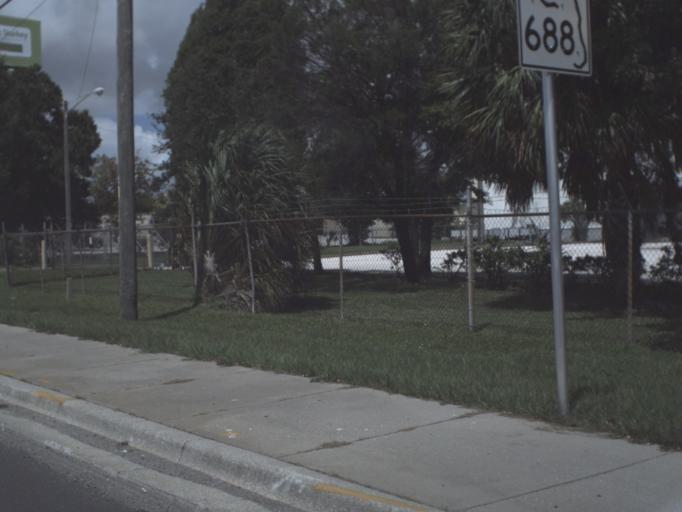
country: US
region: Florida
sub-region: Pinellas County
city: Largo
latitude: 27.8946
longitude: -82.7630
